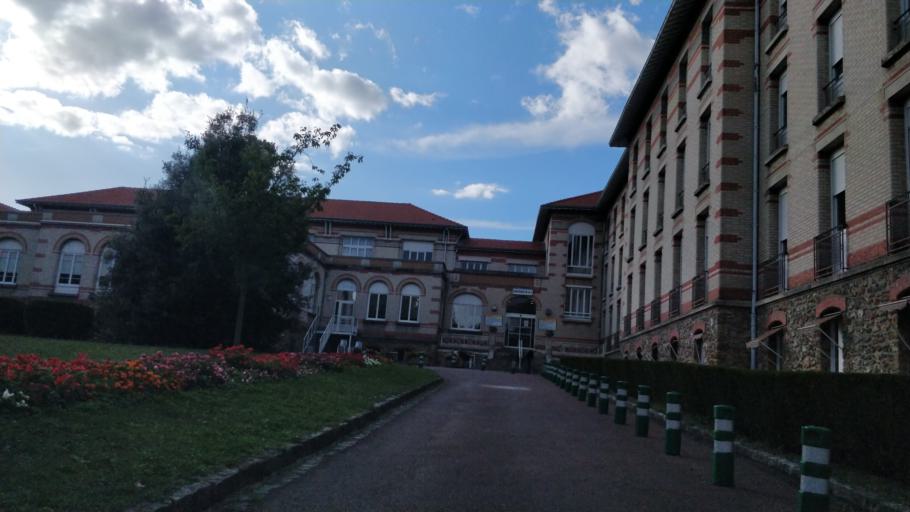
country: FR
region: Ile-de-France
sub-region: Departement de l'Essonne
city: Fontenay-les-Briis
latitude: 48.6231
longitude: 2.1482
